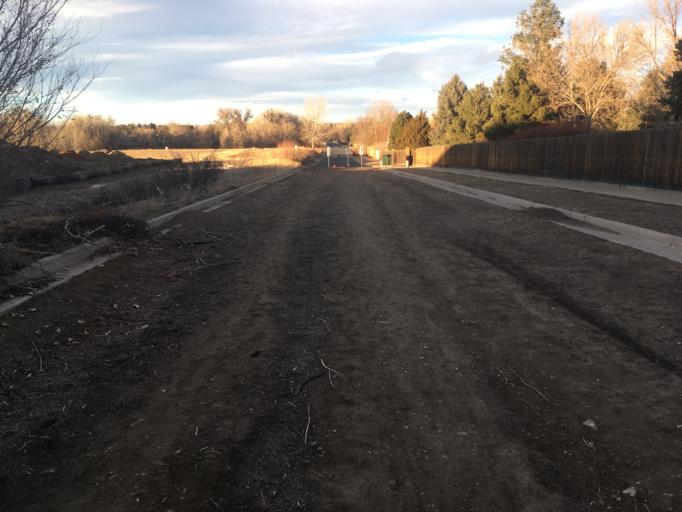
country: US
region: Colorado
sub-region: Jefferson County
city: Applewood
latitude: 39.8192
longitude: -105.1566
